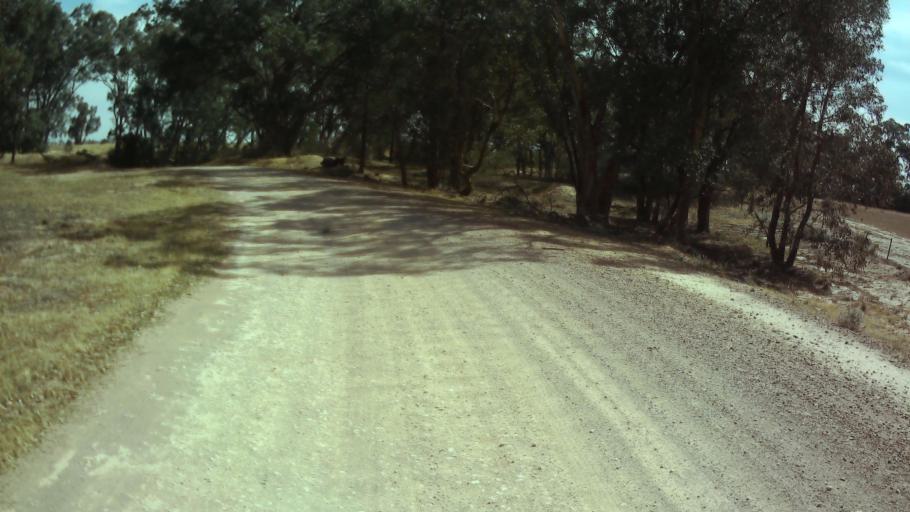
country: AU
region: New South Wales
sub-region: Weddin
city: Grenfell
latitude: -34.0408
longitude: 148.0798
